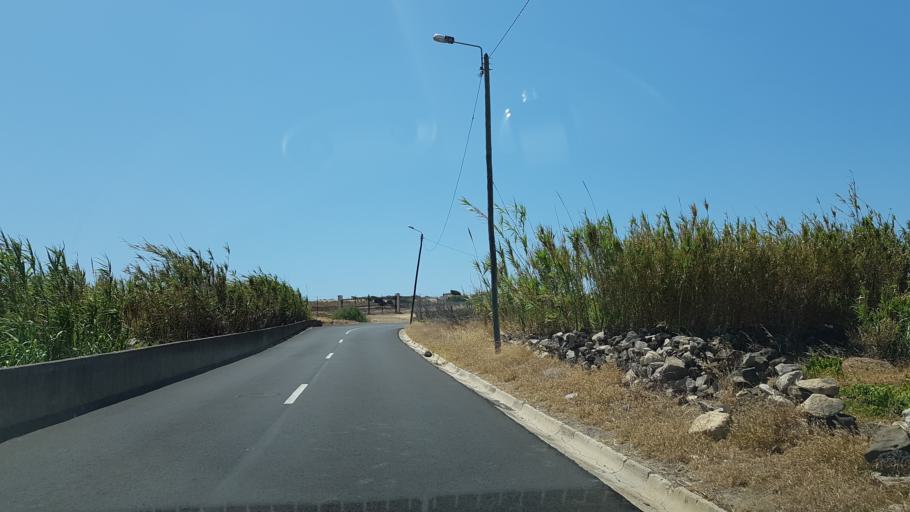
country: PT
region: Madeira
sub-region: Porto Santo
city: Camacha
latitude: 33.0788
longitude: -16.3480
